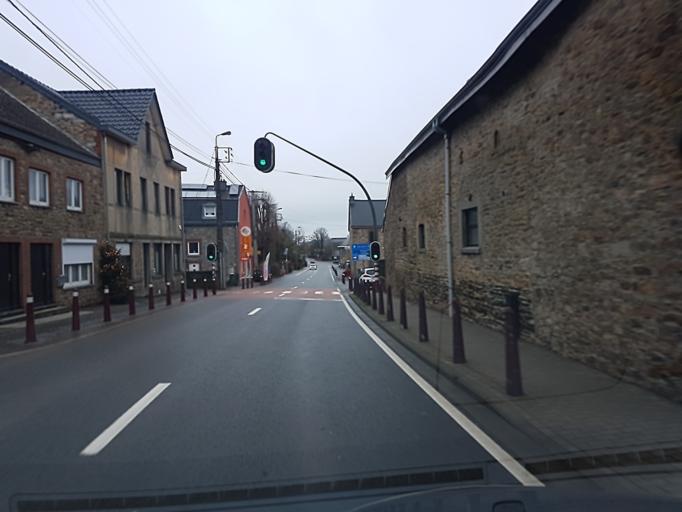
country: BE
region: Wallonia
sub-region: Province de Liege
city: Spa
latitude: 50.5204
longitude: 5.9115
